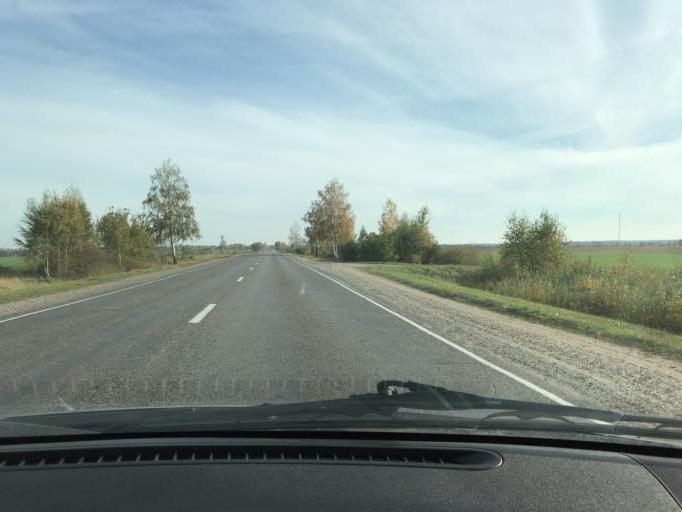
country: BY
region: Brest
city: Asnyezhytsy
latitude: 52.2105
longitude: 26.0481
